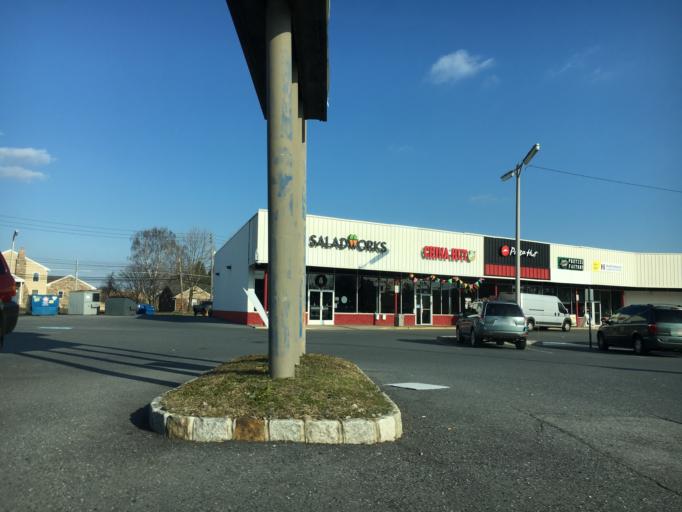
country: US
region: Pennsylvania
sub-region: Lehigh County
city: Hokendauqua
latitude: 40.6424
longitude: -75.4907
